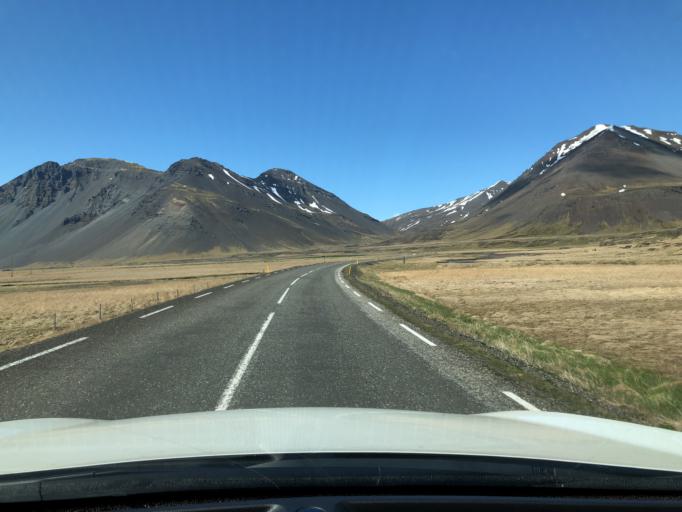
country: IS
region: East
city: Hoefn
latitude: 64.4296
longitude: -14.6347
